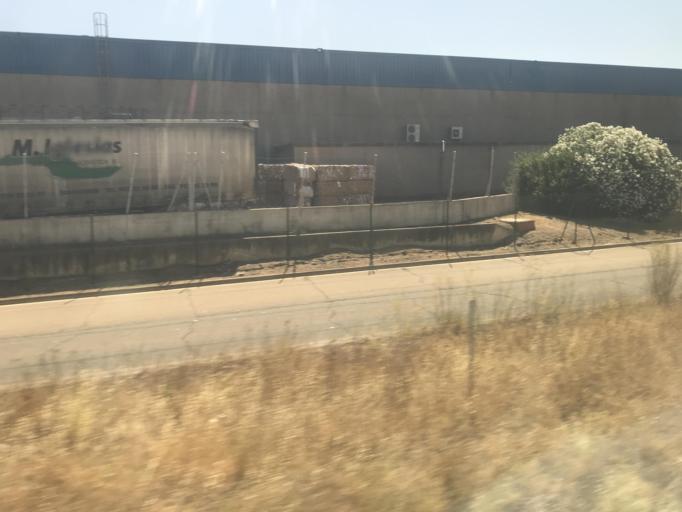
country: ES
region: Castille and Leon
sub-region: Provincia de Palencia
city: Duenas
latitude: 41.8440
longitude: -4.5577
